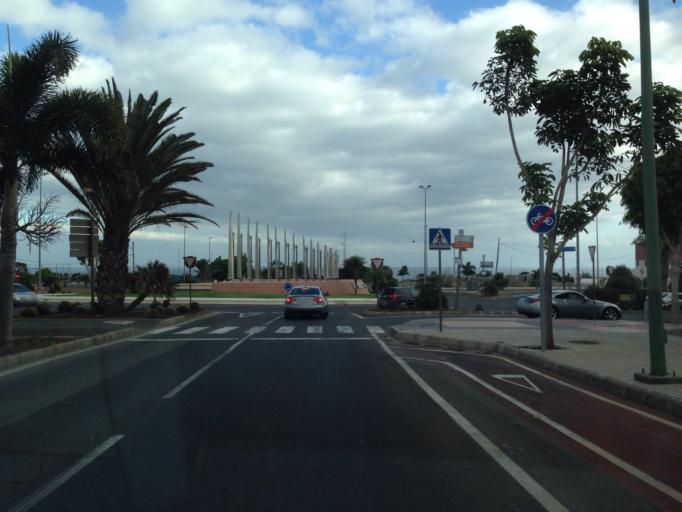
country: ES
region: Canary Islands
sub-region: Provincia de Las Palmas
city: Cruce de Arinaga
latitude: 27.8366
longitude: -15.4507
